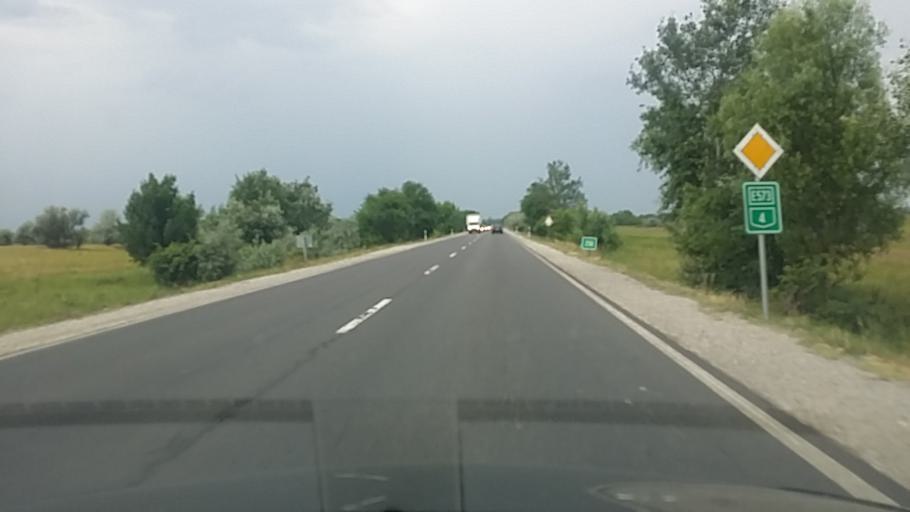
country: HU
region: Szabolcs-Szatmar-Bereg
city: Ujfeherto
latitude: 47.7902
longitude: 21.6953
